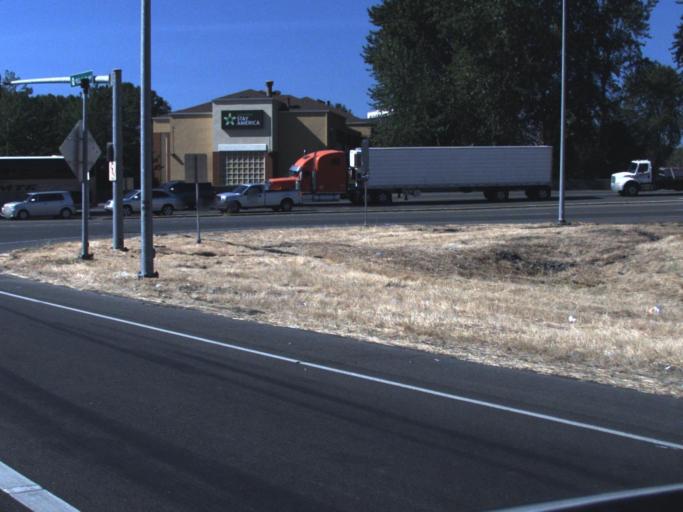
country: US
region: Washington
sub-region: King County
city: Tukwila
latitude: 47.4629
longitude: -122.2452
